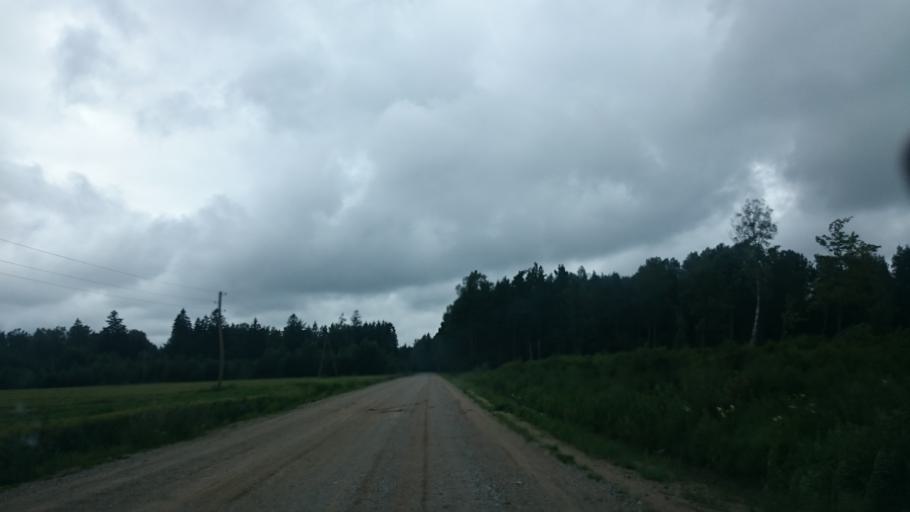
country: LV
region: Pavilostas
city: Pavilosta
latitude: 56.8557
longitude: 21.2380
